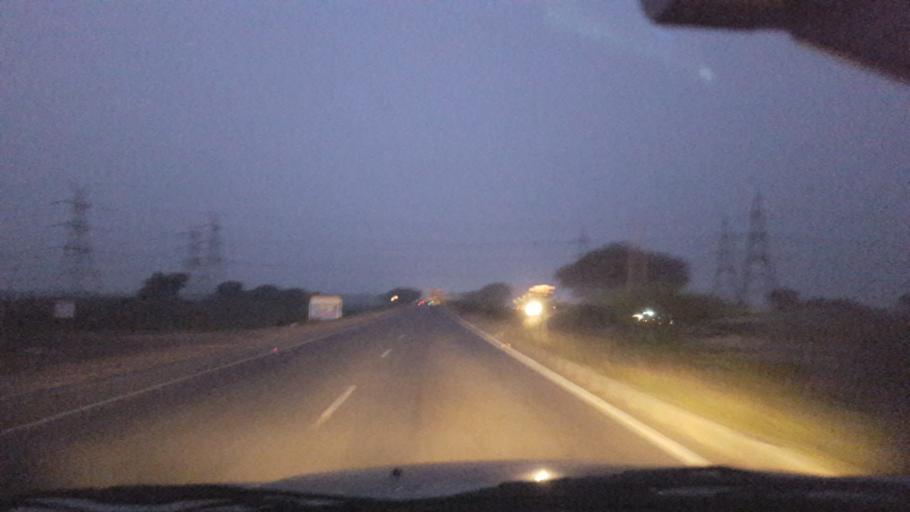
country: IN
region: Andhra Pradesh
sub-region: East Godavari
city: Rajahmundry
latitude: 17.1071
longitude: 81.9200
